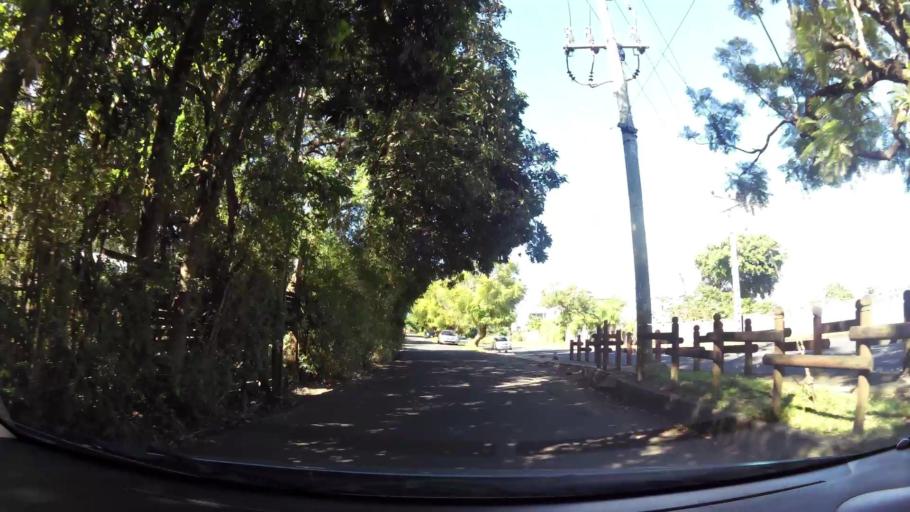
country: MU
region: Plaines Wilhems
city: Vacoas
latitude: -20.2997
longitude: 57.4945
